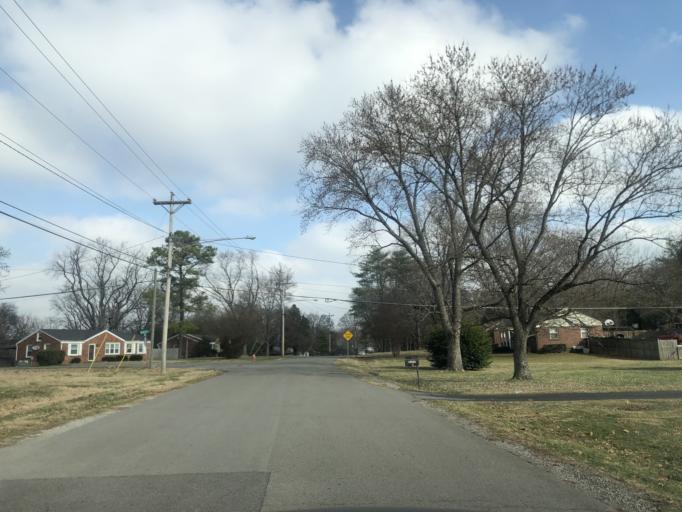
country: US
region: Tennessee
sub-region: Davidson County
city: Oak Hill
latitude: 36.0968
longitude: -86.7215
